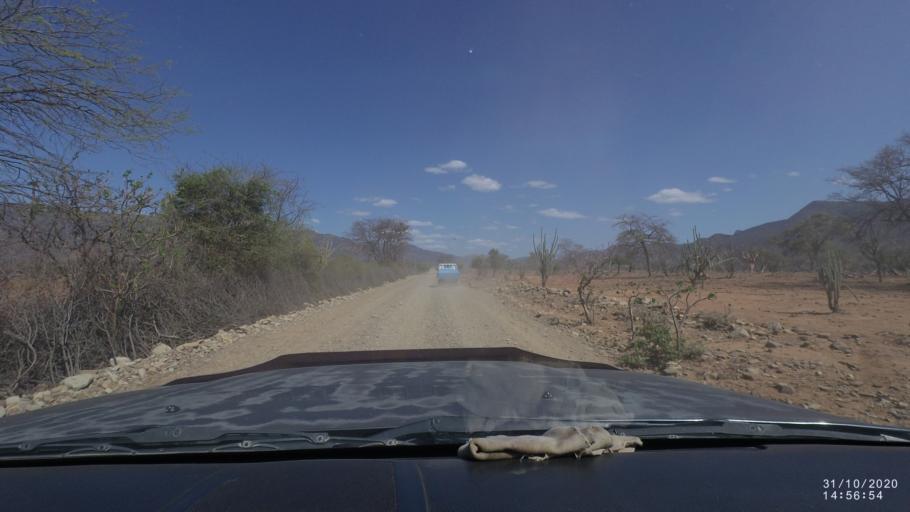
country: BO
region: Cochabamba
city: Aiquile
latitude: -18.2411
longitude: -64.8467
